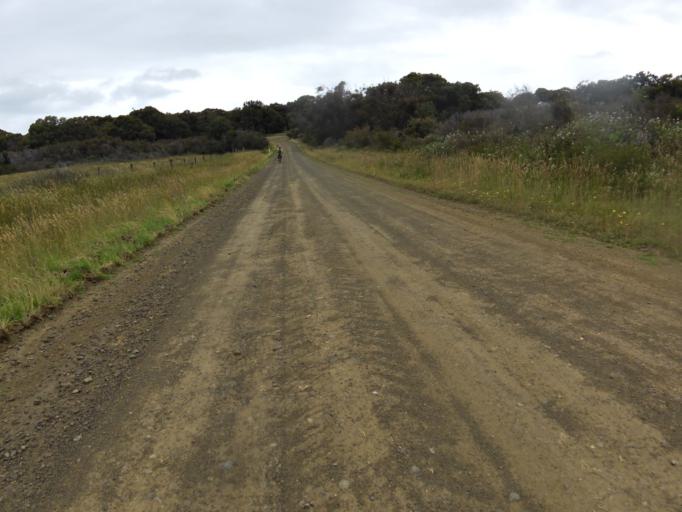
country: AU
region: Victoria
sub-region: Bass Coast
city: Cowes
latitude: -38.3878
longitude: 145.3864
